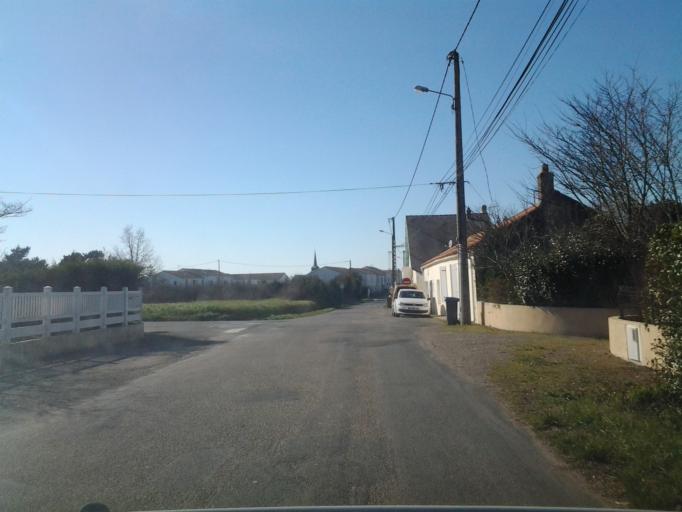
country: FR
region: Pays de la Loire
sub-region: Departement de la Vendee
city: Olonne-sur-Mer
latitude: 46.5377
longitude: -1.7656
